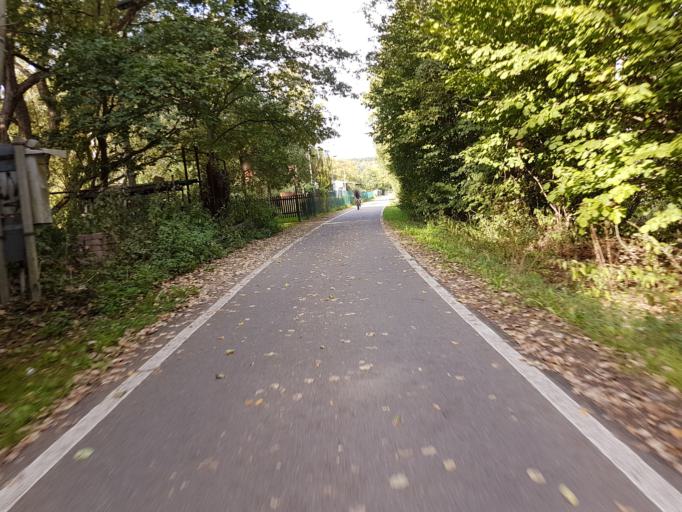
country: DE
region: Saxony
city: Wittgensdorf
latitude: 50.8893
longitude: 12.8904
